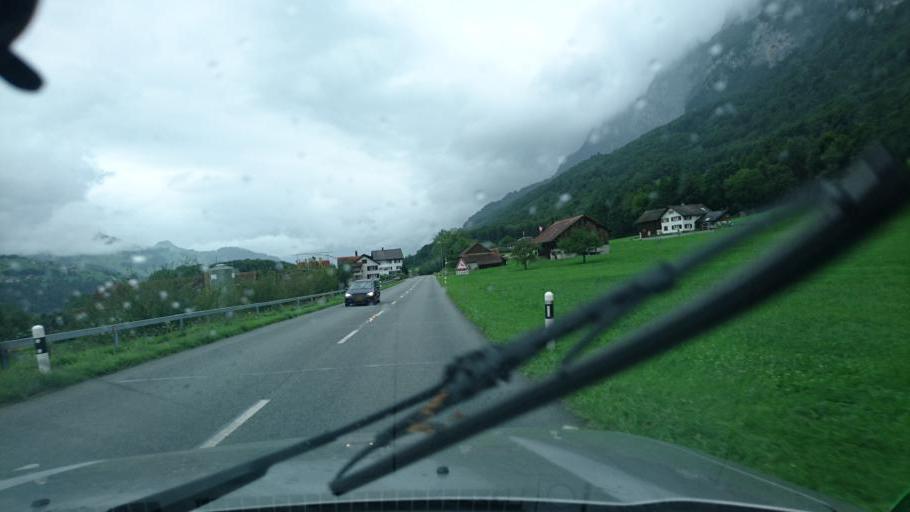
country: CH
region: Saint Gallen
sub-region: Wahlkreis Sarganserland
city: Sargans
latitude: 47.0717
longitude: 9.3928
